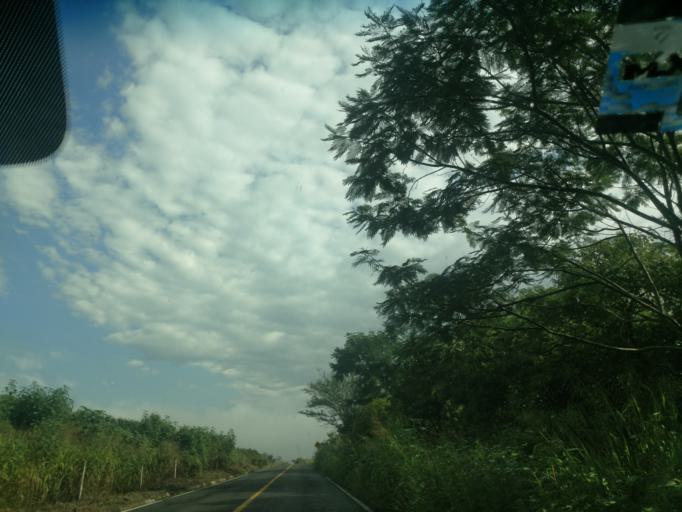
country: MX
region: Jalisco
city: Ameca
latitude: 20.5255
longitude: -104.1267
